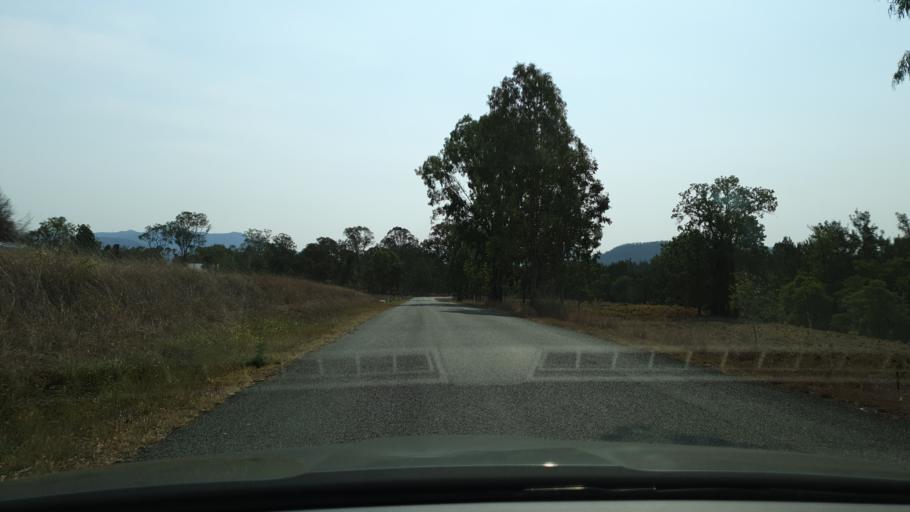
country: AU
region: Queensland
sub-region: Ipswich
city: Deebing Heights
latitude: -28.1378
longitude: 152.5897
